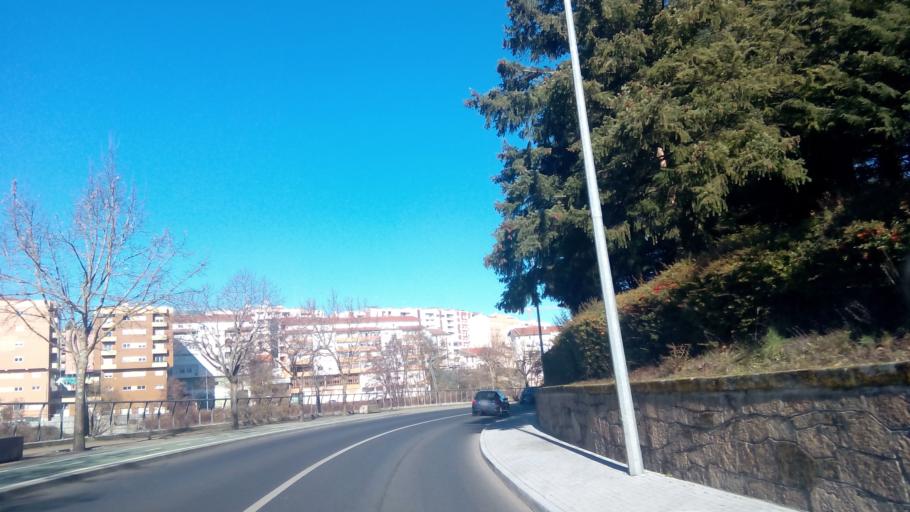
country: PT
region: Braganca
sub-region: Braganca Municipality
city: Braganca
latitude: 41.7990
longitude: -6.7623
